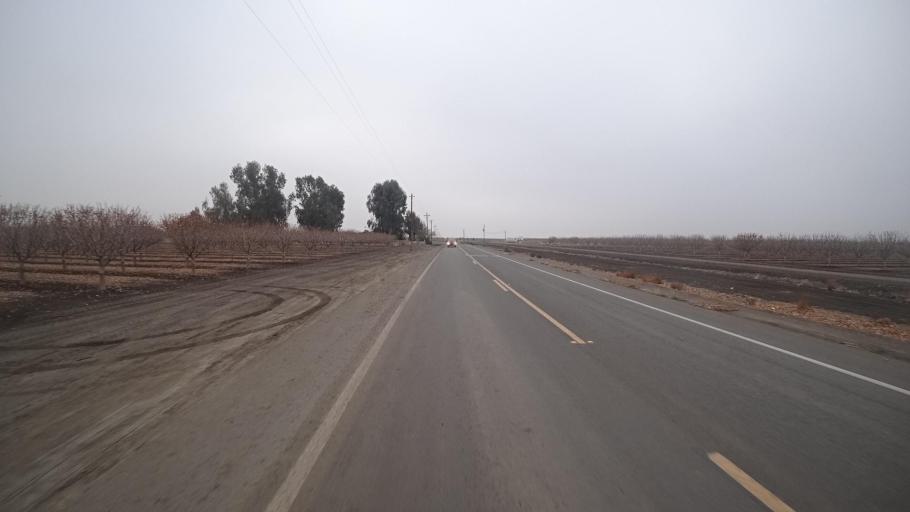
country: US
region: California
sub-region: Kern County
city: Buttonwillow
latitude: 35.3691
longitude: -119.4724
